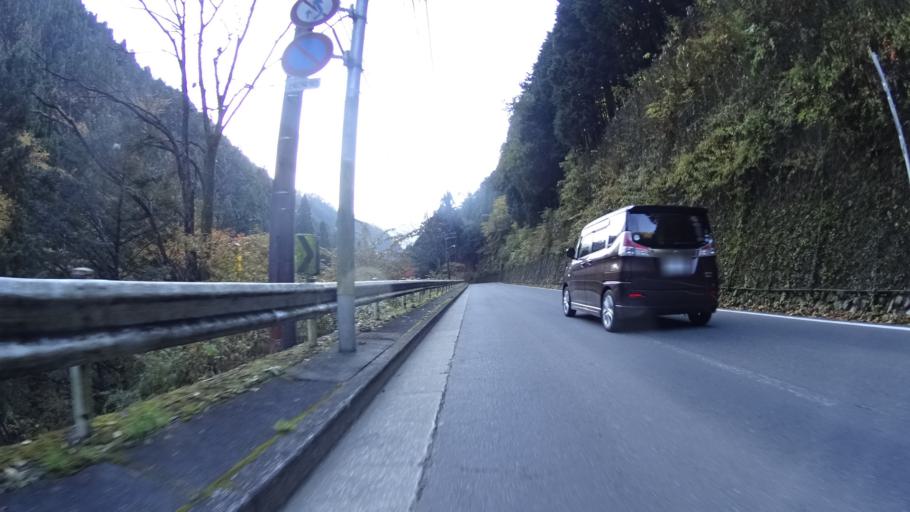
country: JP
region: Tokyo
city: Itsukaichi
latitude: 35.7100
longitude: 139.1518
